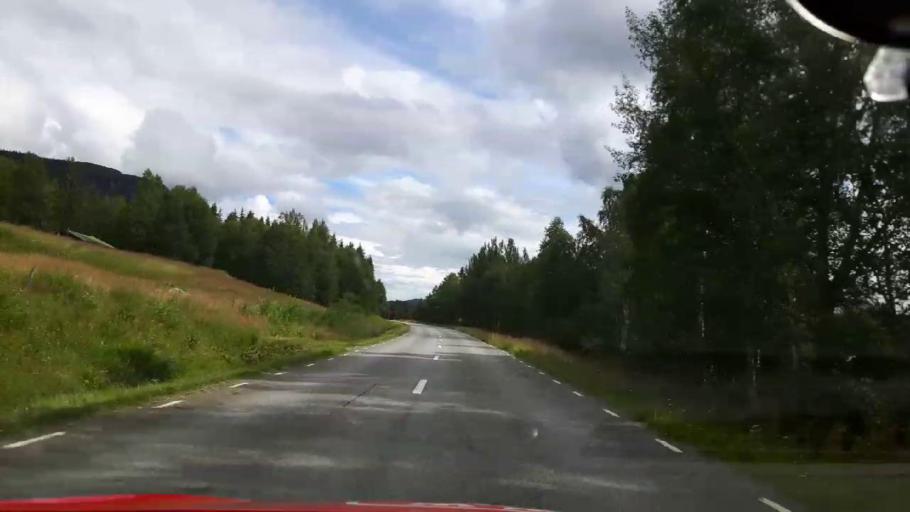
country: NO
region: Nord-Trondelag
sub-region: Lierne
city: Sandvika
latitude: 64.3898
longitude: 14.4081
